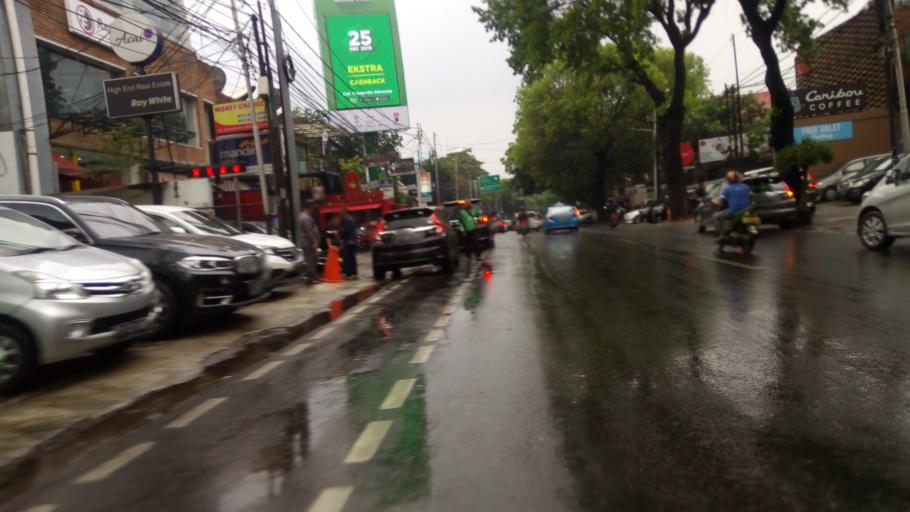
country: ID
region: Jakarta Raya
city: Jakarta
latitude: -6.2308
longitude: 106.8082
